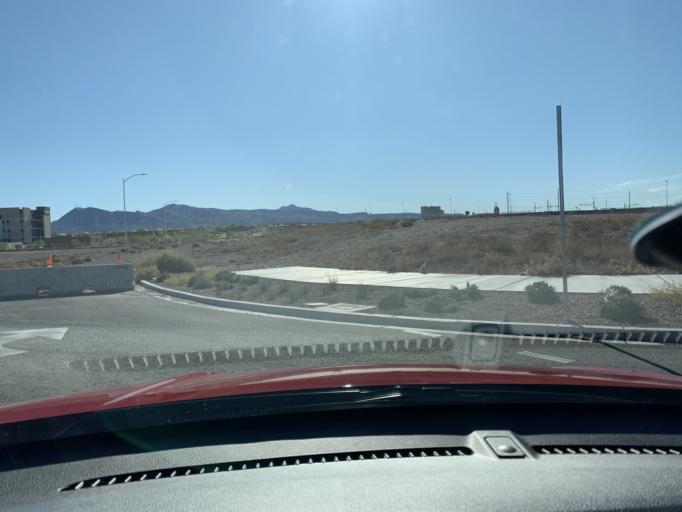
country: US
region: Nevada
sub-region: Clark County
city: Whitney
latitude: 36.0759
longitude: -115.0330
